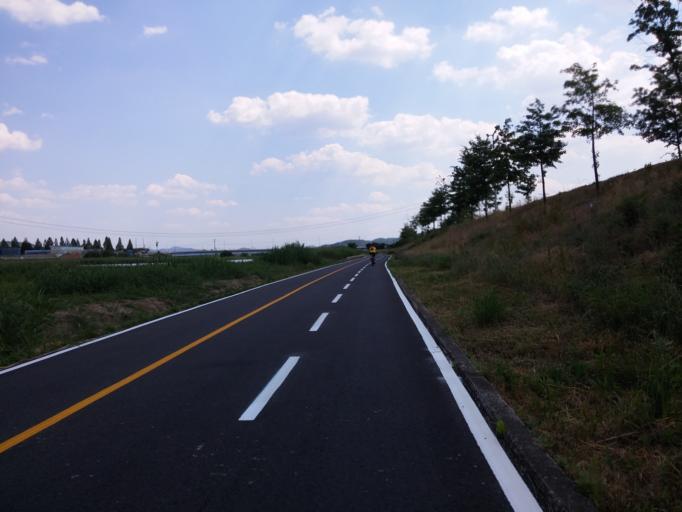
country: KR
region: Chungcheongbuk-do
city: Cheongju-si
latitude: 36.6016
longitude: 127.4978
